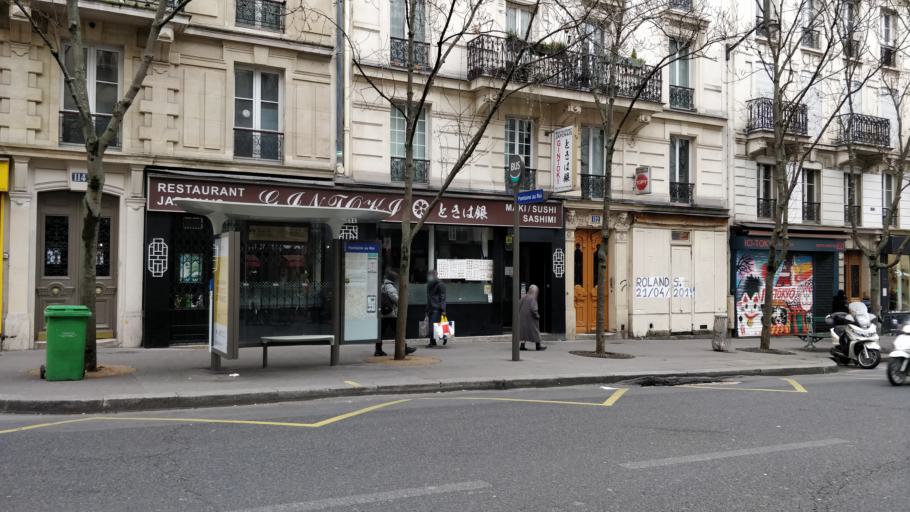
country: FR
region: Ile-de-France
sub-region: Paris
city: Paris
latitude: 48.8673
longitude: 2.3730
